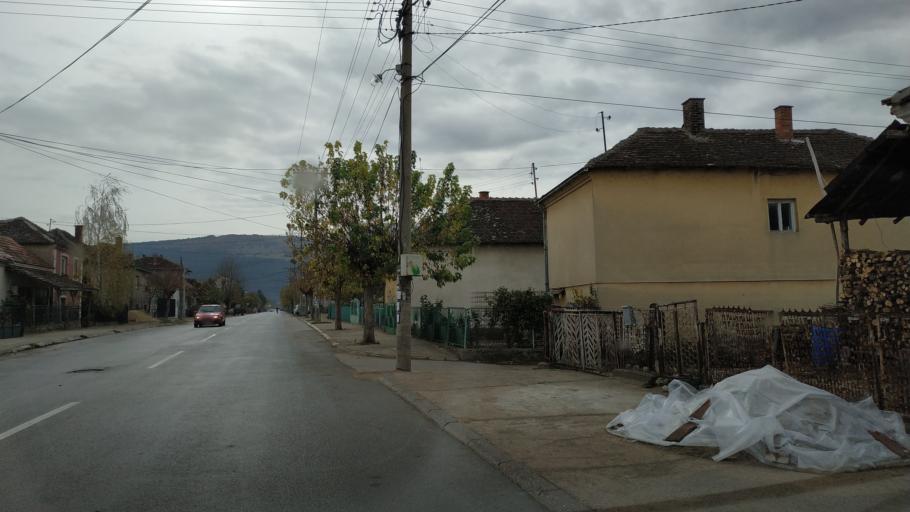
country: RS
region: Central Serbia
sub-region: Pirotski Okrug
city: Bela Palanka
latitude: 43.2289
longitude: 22.3171
